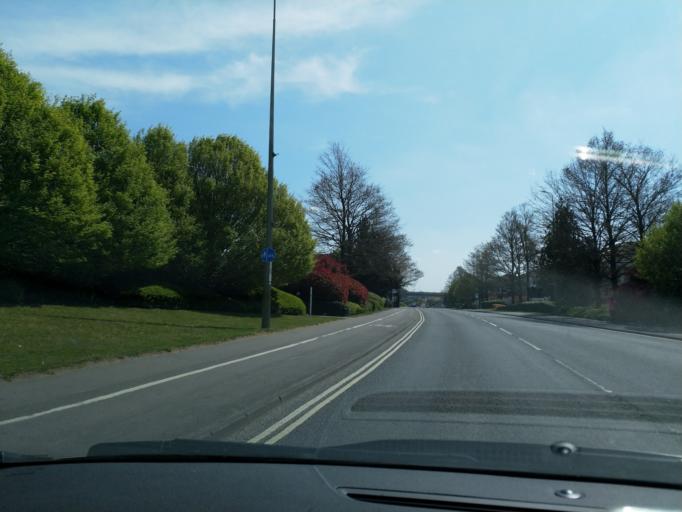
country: GB
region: England
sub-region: Oxfordshire
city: Cowley
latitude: 51.7319
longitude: -1.2060
